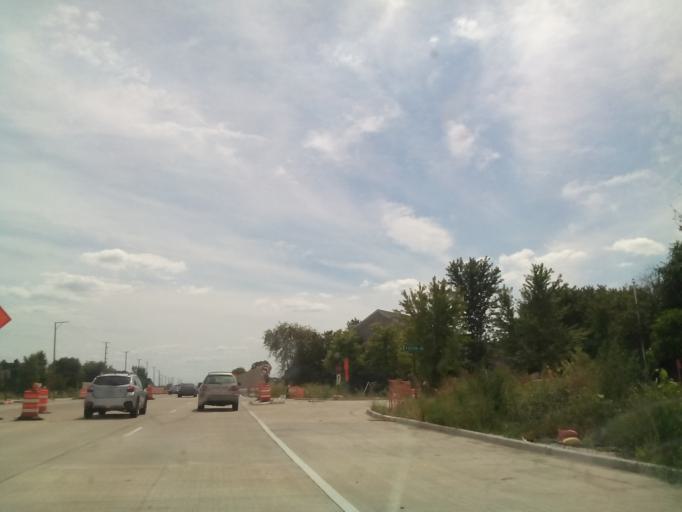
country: US
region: Illinois
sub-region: DuPage County
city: Warrenville
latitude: 41.7888
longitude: -88.2057
